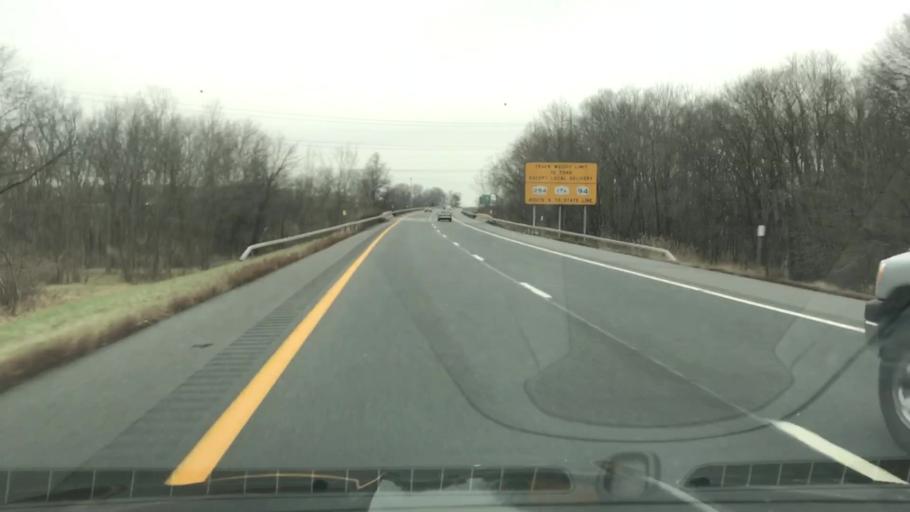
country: US
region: New York
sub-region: Orange County
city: Mechanicstown
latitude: 41.4238
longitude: -74.3997
